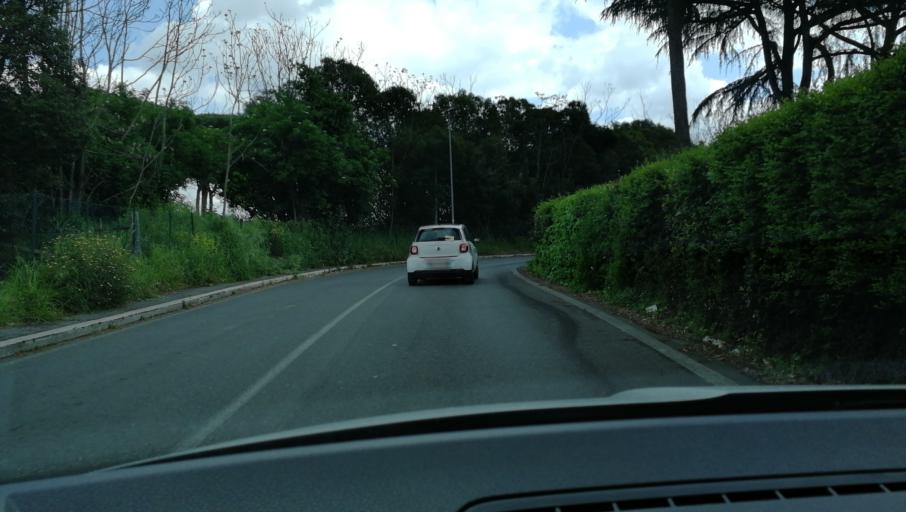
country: IT
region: Latium
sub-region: Citta metropolitana di Roma Capitale
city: Rome
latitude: 41.8611
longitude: 12.5343
